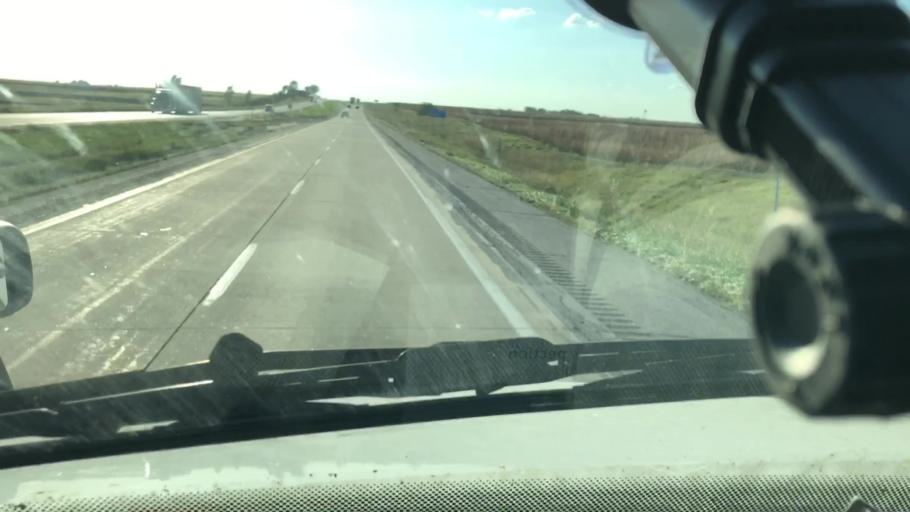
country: US
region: Iowa
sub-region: Pottawattamie County
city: Avoca
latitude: 41.4994
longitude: -95.4993
